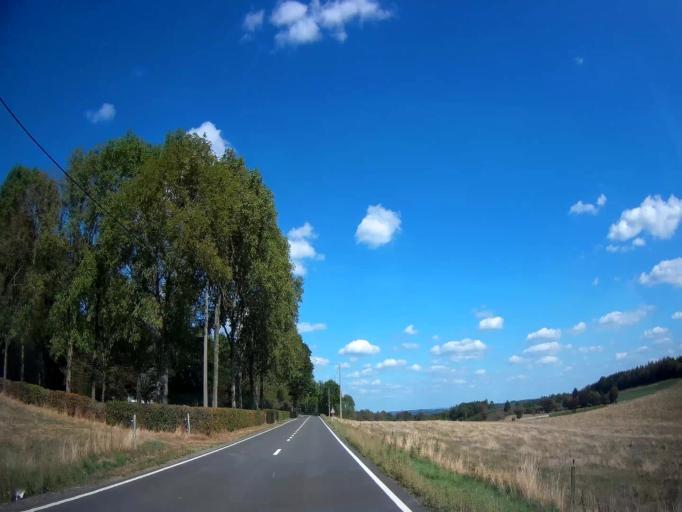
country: BE
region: Wallonia
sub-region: Province de Namur
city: Beauraing
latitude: 50.1820
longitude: 4.9274
